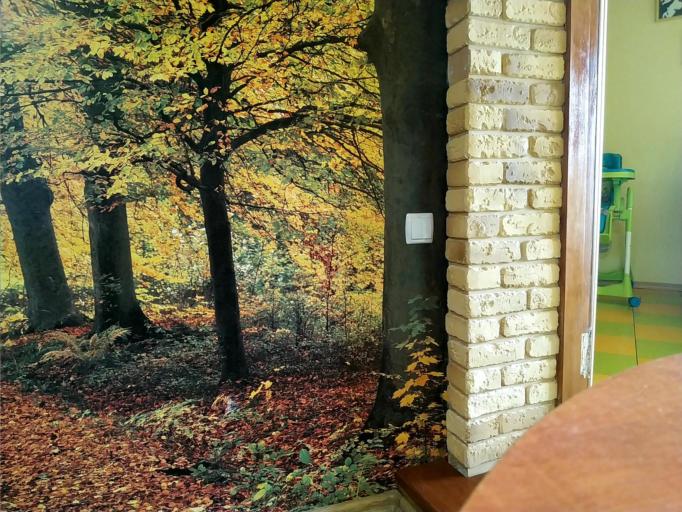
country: RU
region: Smolensk
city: Ozernyy
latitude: 55.4358
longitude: 32.6970
